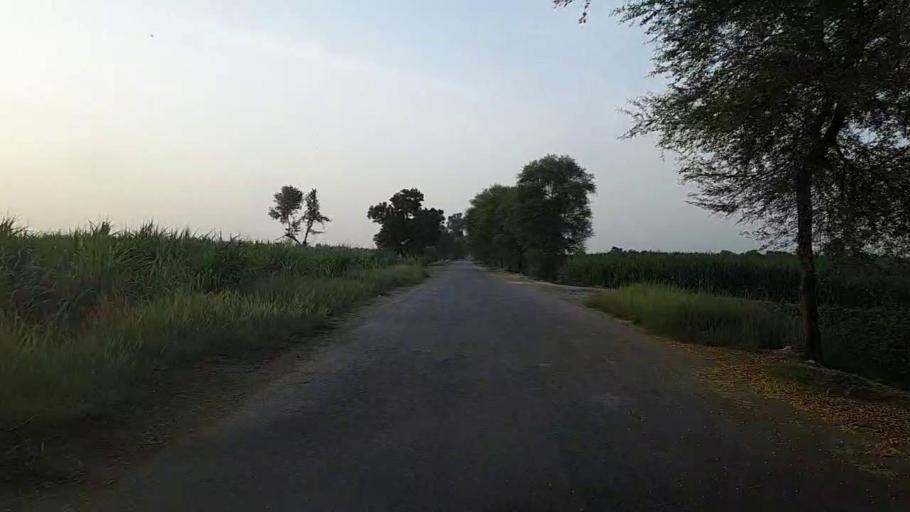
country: PK
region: Sindh
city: Ubauro
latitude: 28.2441
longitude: 69.8106
